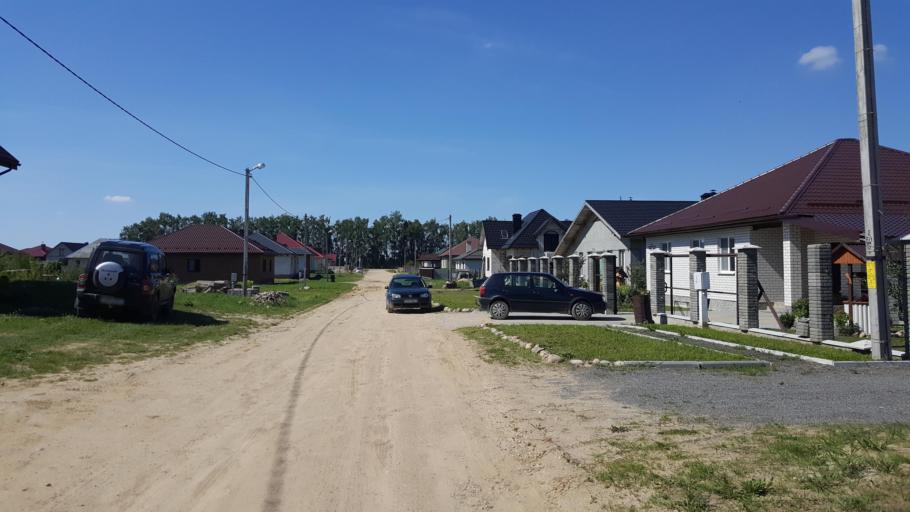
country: BY
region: Brest
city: Charnawchytsy
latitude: 52.2571
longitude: 23.5891
